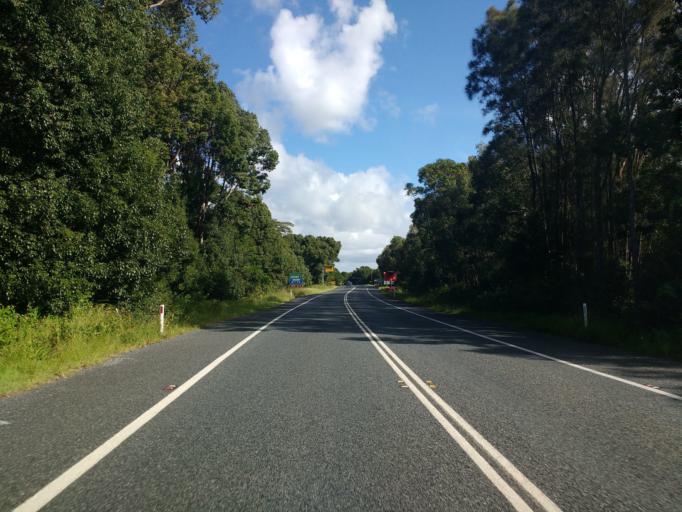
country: AU
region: New South Wales
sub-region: Ballina
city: Ballina
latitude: -28.9472
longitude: 153.4669
